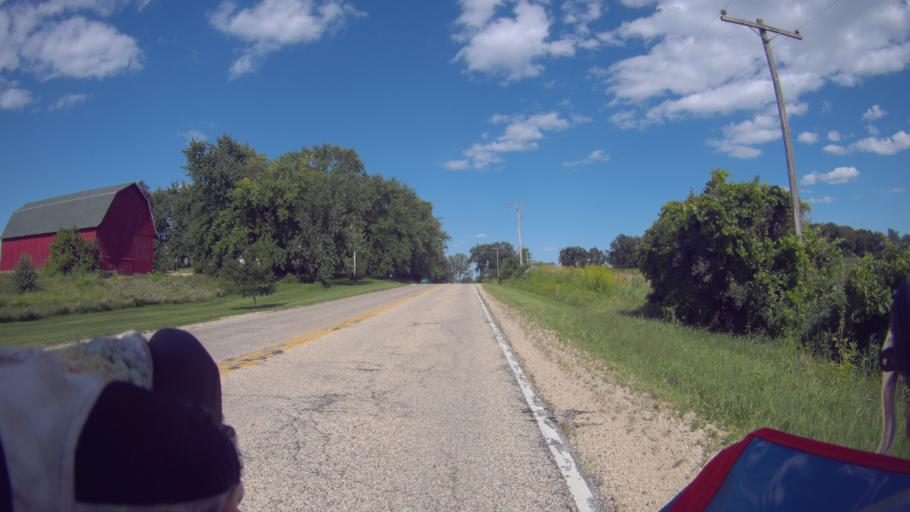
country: US
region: Wisconsin
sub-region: Green County
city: Brooklyn
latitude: 42.8965
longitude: -89.3269
